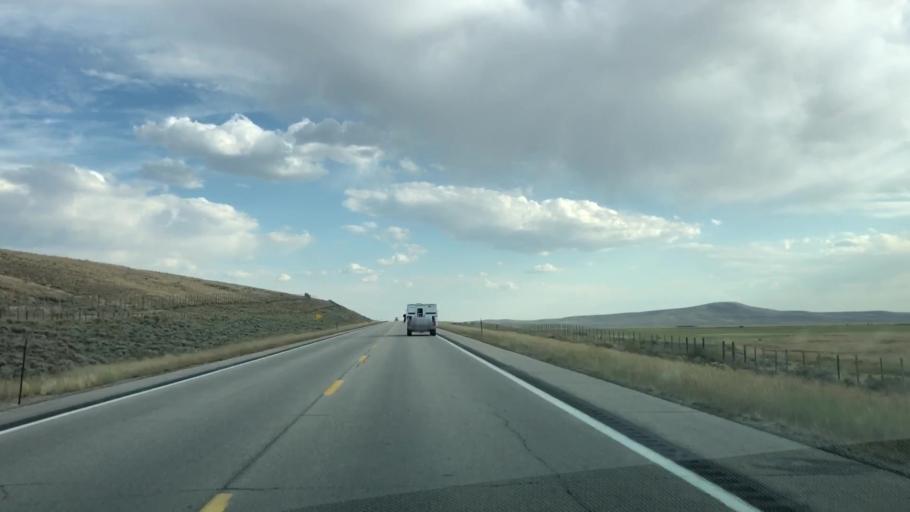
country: US
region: Wyoming
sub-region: Sublette County
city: Pinedale
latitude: 42.9489
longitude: -110.0855
